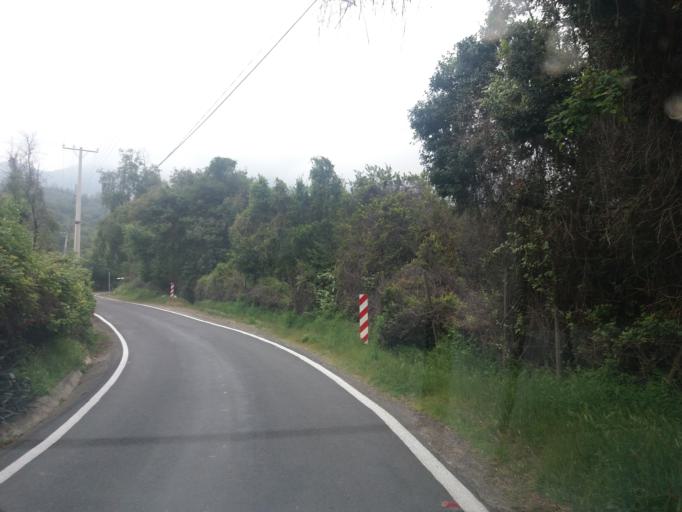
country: CL
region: Valparaiso
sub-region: Provincia de Marga Marga
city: Limache
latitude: -33.0204
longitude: -71.0715
